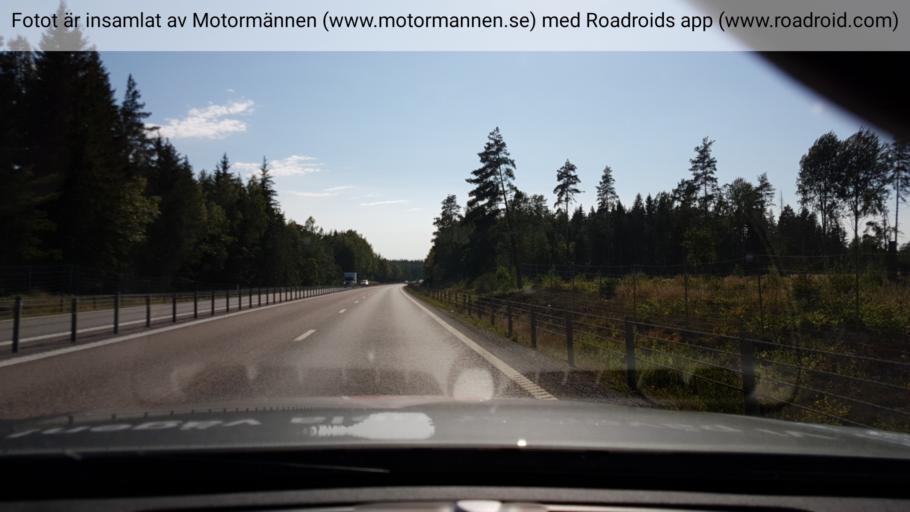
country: SE
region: Vaestmanland
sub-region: Hallstahammars Kommun
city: Hallstahammar
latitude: 59.5781
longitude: 16.1373
